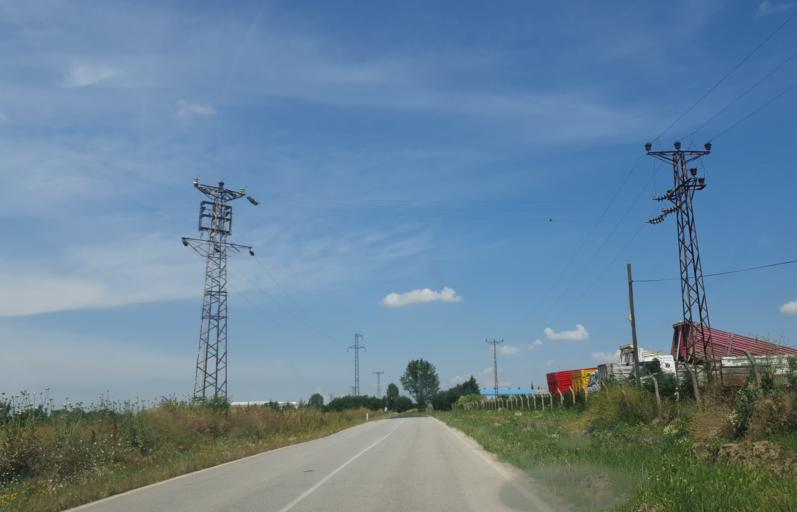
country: TR
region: Tekirdag
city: Muratli
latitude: 41.2044
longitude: 27.5231
